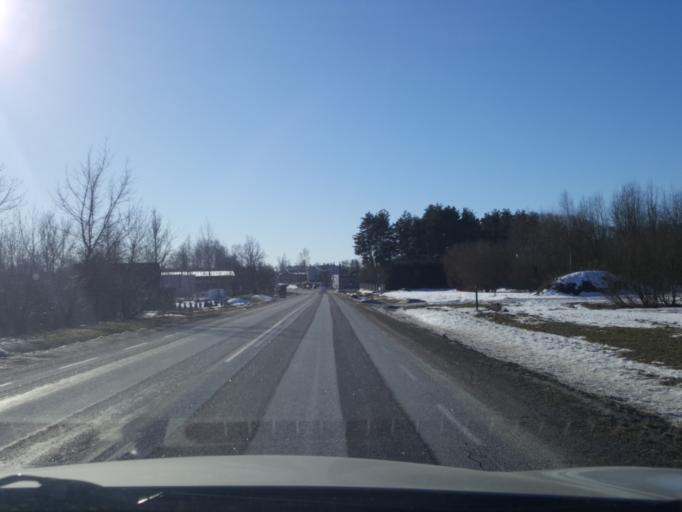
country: EE
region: Viljandimaa
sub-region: Viljandi linn
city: Viljandi
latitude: 58.3803
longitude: 25.6034
